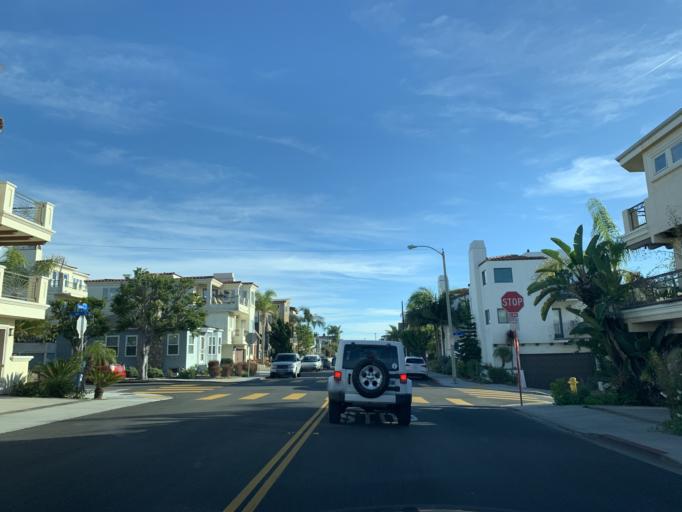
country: US
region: California
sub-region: Los Angeles County
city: Manhattan Beach
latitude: 33.8783
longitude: -118.4063
